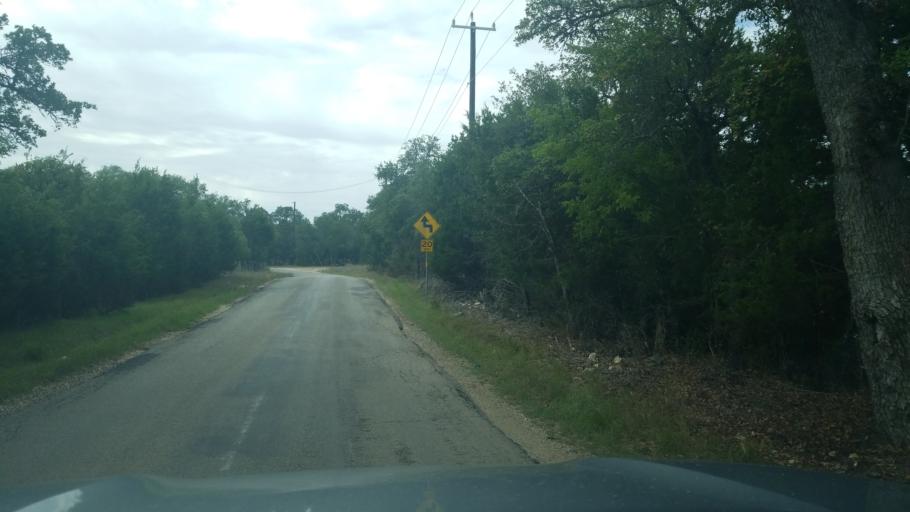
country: US
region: Texas
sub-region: Comal County
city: Bulverde
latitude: 29.7688
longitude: -98.4138
